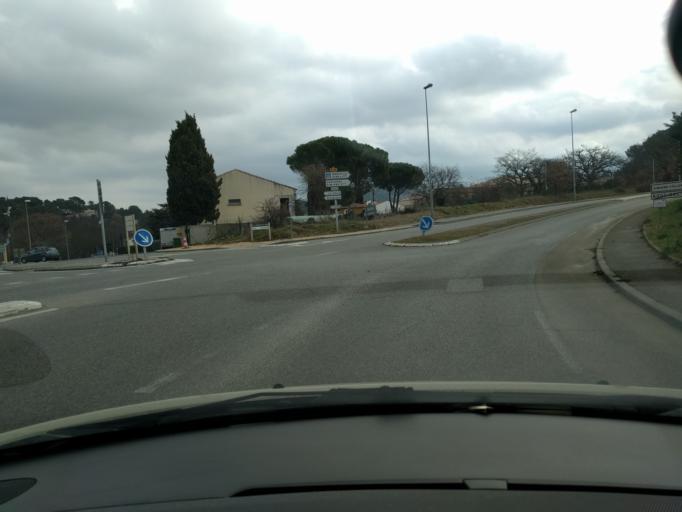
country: FR
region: Provence-Alpes-Cote d'Azur
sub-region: Departement des Bouches-du-Rhone
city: Simiane-Collongue
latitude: 43.4373
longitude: 5.4240
